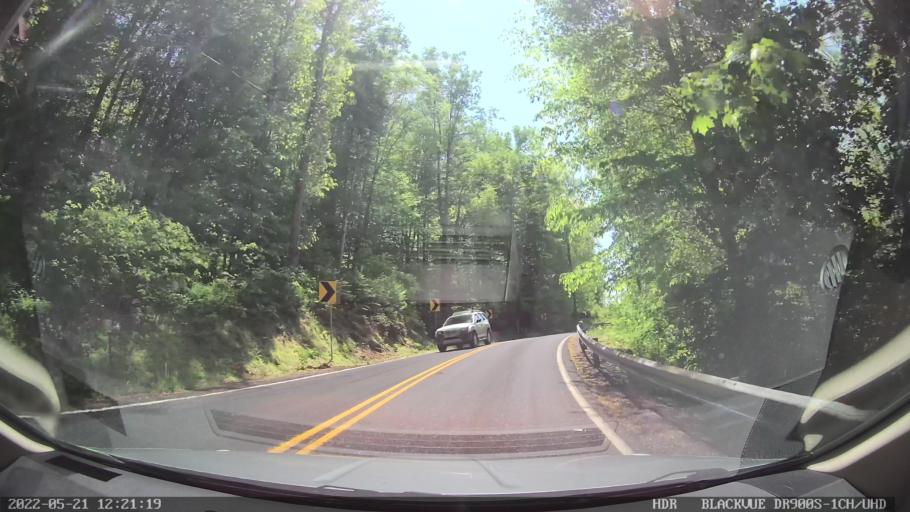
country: US
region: Pennsylvania
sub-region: Berks County
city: Bally
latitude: 40.4075
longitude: -75.6139
